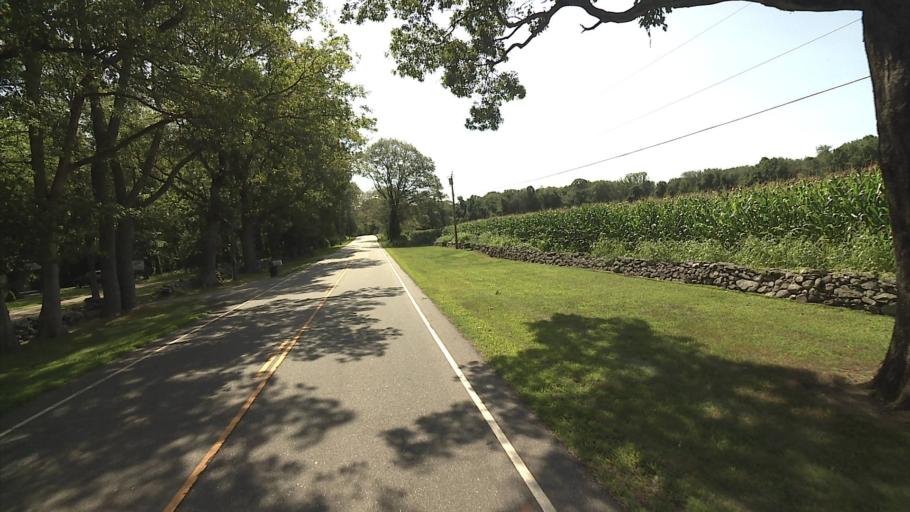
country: US
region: Connecticut
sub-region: Tolland County
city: Hebron
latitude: 41.6333
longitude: -72.3206
